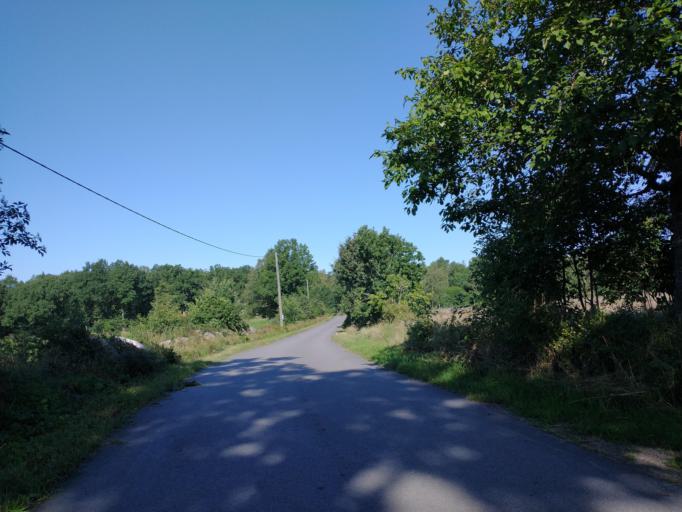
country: SE
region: Kalmar
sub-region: Kalmar Kommun
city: Lindsdal
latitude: 56.7828
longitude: 16.2790
